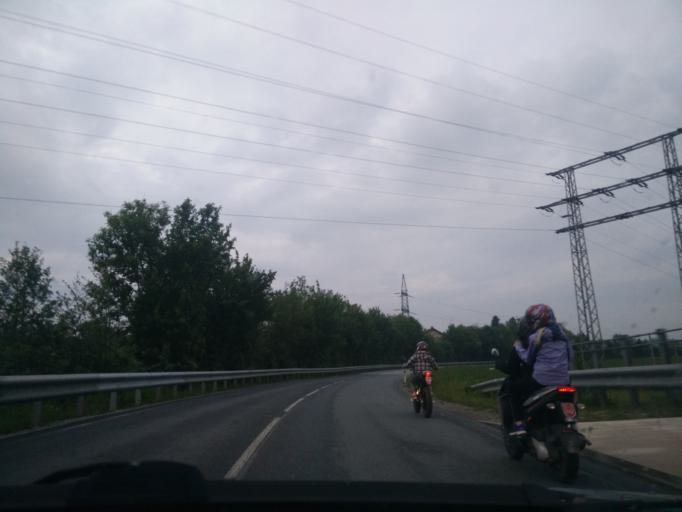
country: AT
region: Salzburg
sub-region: Politischer Bezirk Salzburg-Umgebung
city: Seekirchen am Wallersee
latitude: 47.8892
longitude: 13.1195
